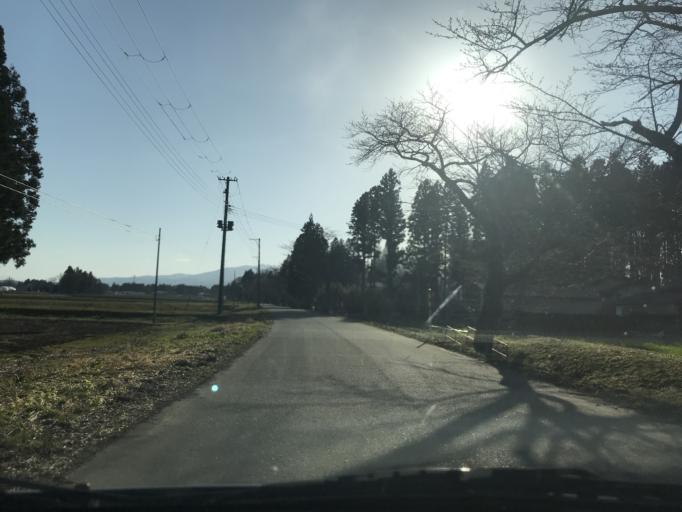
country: JP
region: Iwate
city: Kitakami
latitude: 39.2606
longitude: 141.0446
